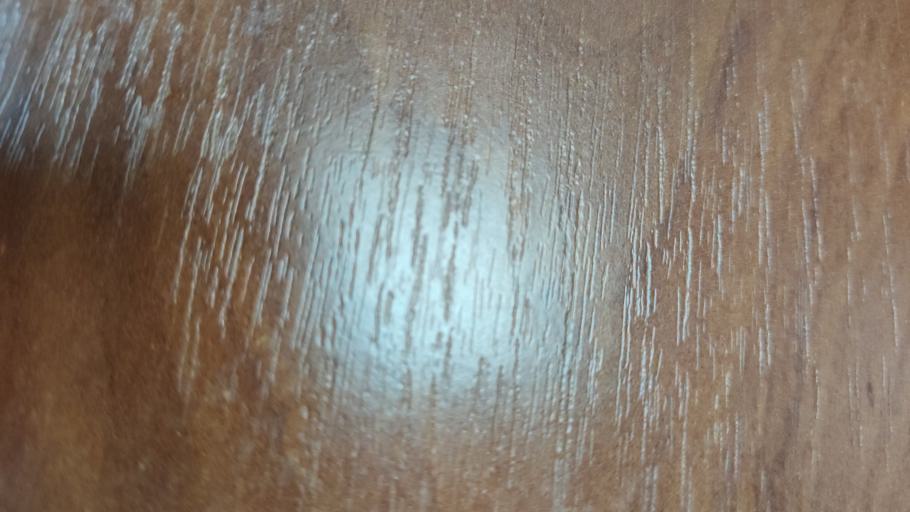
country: RU
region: Moskovskaya
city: Peshki
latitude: 56.1607
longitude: 37.0343
